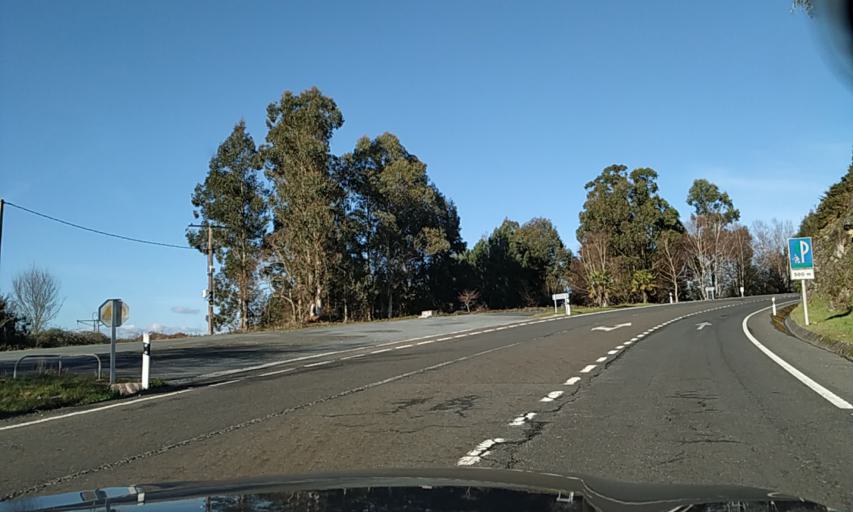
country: ES
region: Galicia
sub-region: Provincia da Coruna
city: Ribeira
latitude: 42.7103
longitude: -8.3850
